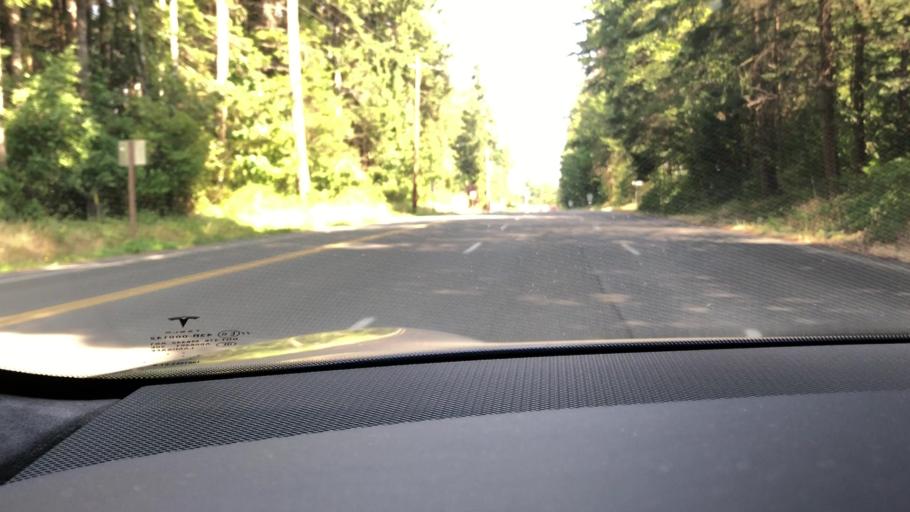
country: US
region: Washington
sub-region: Whatcom County
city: Point Roberts
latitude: 48.9978
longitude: -123.0679
